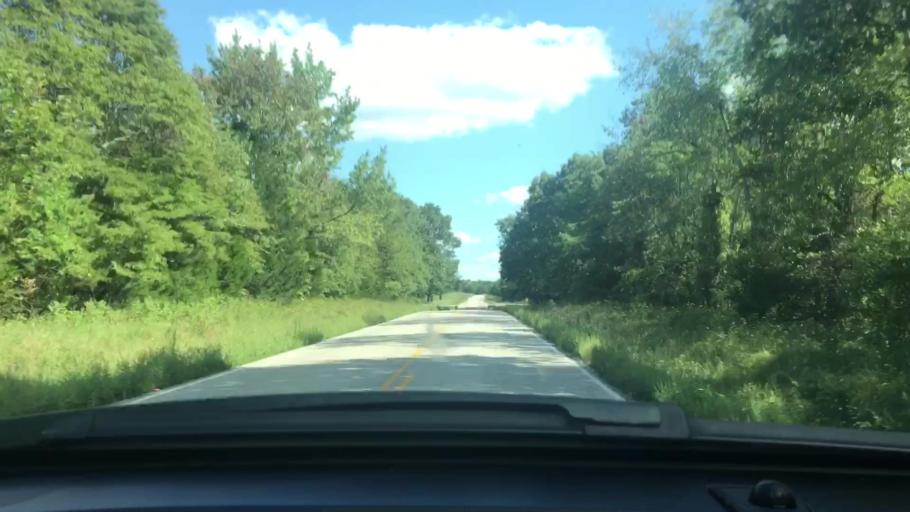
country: US
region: Missouri
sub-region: Wright County
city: Hartville
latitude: 37.3825
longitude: -92.4392
